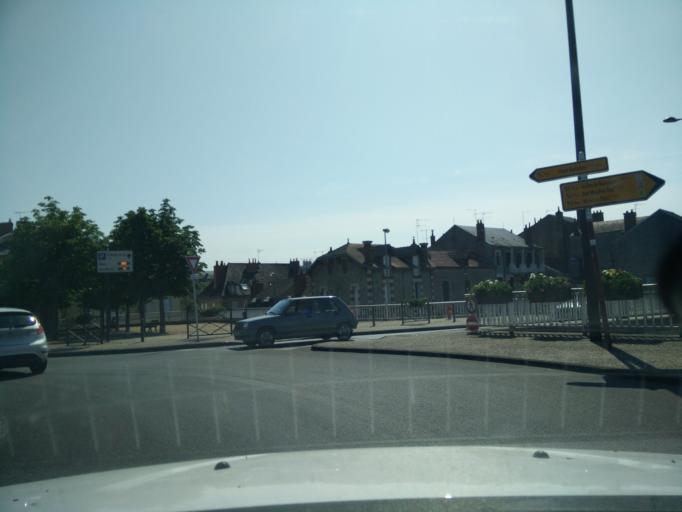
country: FR
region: Auvergne
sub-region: Departement de l'Allier
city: Moulins
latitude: 46.5624
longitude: 3.3252
